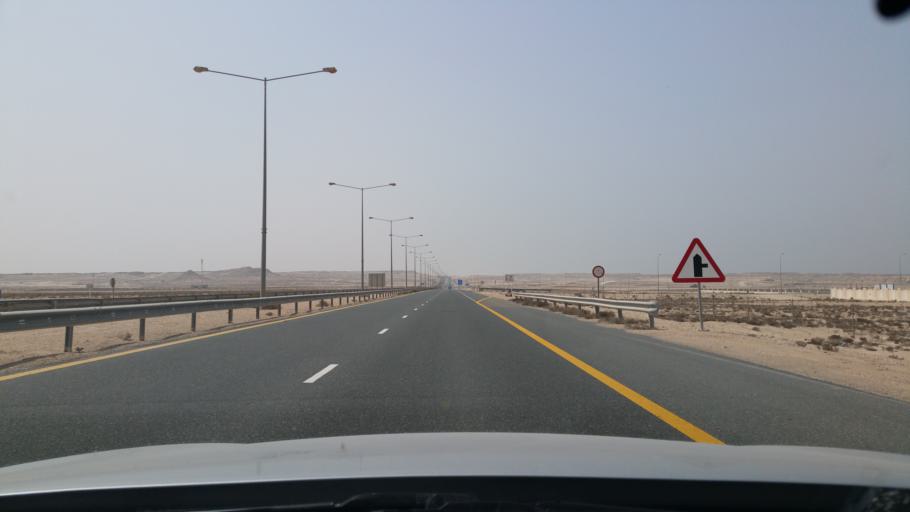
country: QA
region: Baladiyat ar Rayyan
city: Dukhan
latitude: 25.3771
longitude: 50.7811
